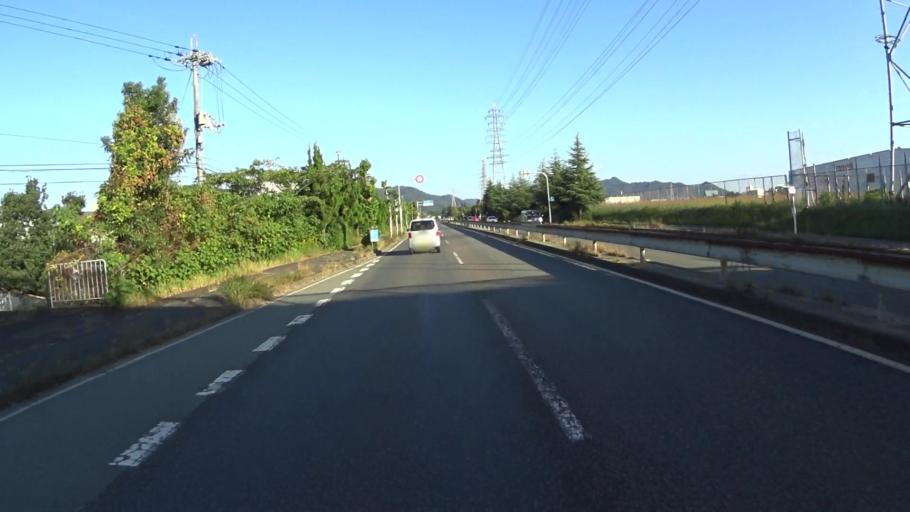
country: JP
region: Kyoto
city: Fukuchiyama
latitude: 35.2895
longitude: 135.1671
